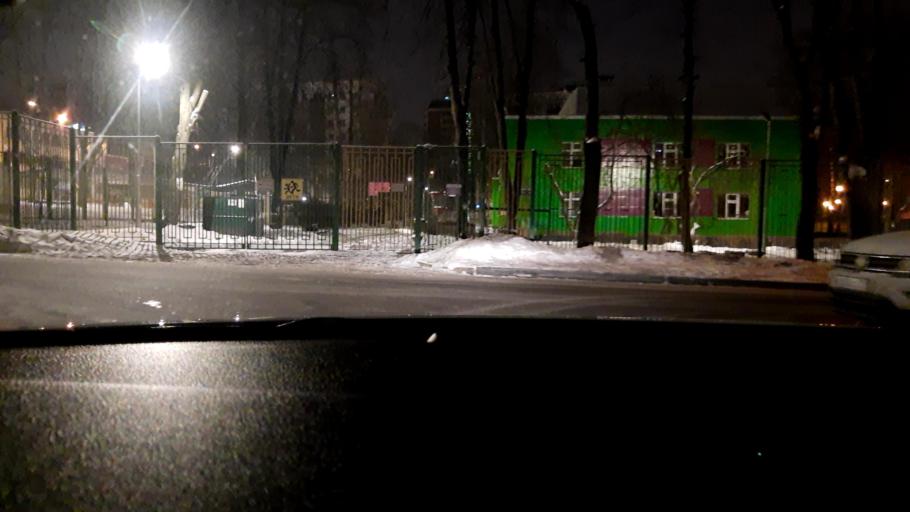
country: RU
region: Moscow
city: Leonovo
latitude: 55.8861
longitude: 37.6487
